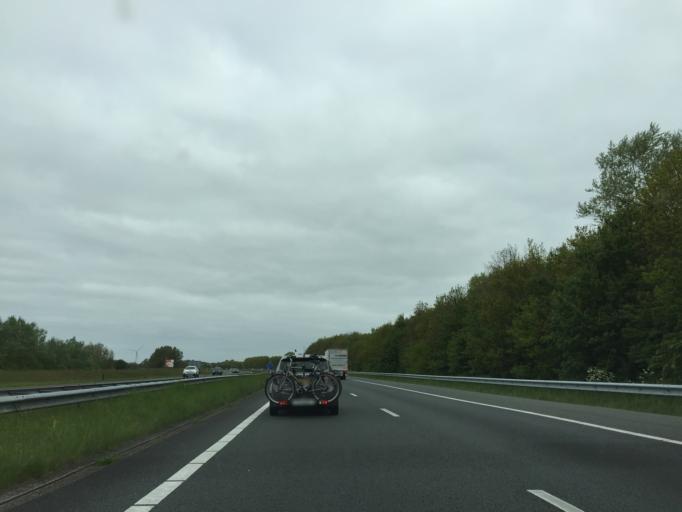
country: NL
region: North Holland
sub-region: Gemeente Hollands Kroon
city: Den Oever
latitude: 52.9185
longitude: 5.0356
